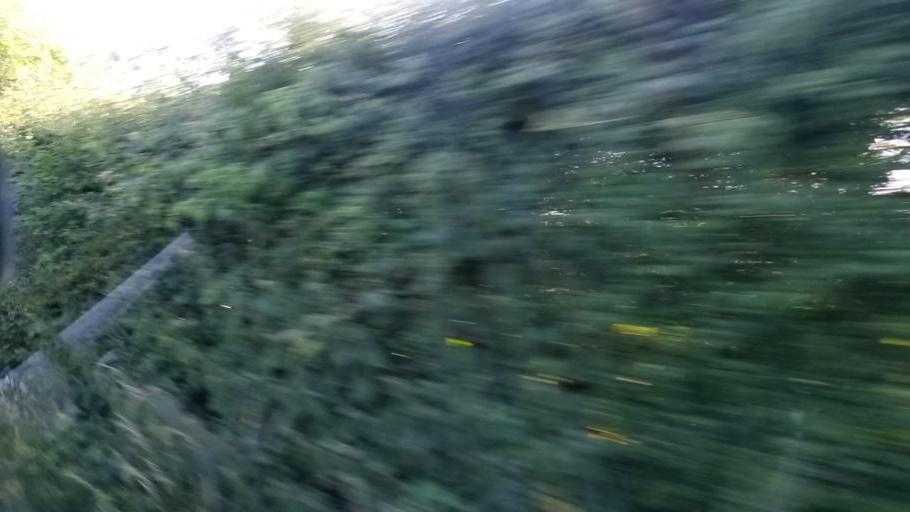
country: IE
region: Leinster
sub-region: An Mhi
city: Ashbourne
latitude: 53.5539
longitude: -6.3806
